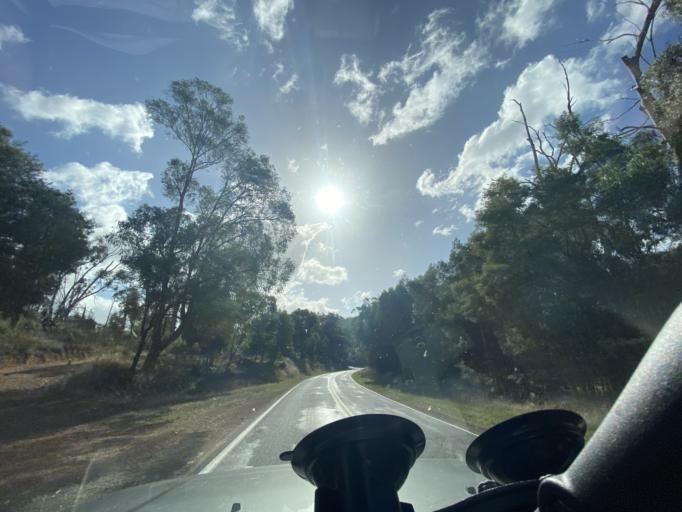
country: AU
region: Victoria
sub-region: Murrindindi
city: Kinglake West
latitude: -37.3268
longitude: 145.3265
